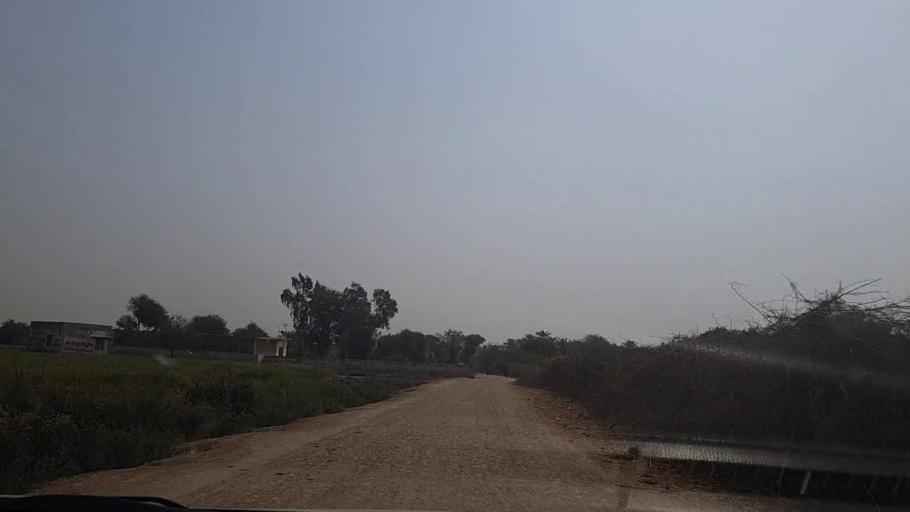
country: PK
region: Sindh
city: Pithoro
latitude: 25.5490
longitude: 69.2495
